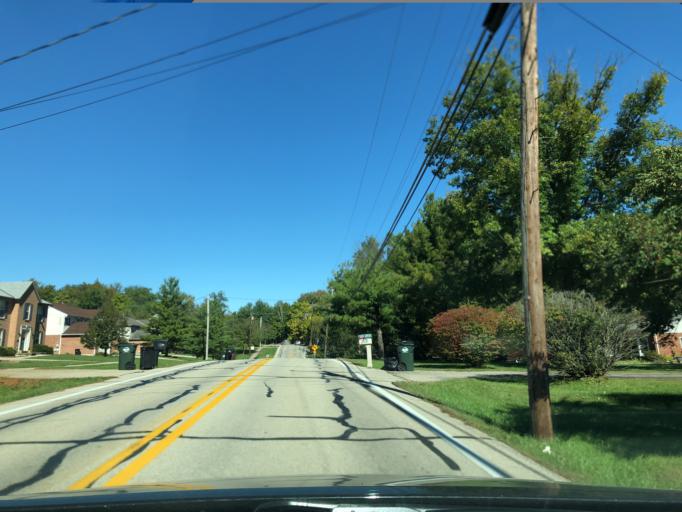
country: US
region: Ohio
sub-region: Hamilton County
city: Sixteen Mile Stand
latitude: 39.2724
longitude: -84.3063
